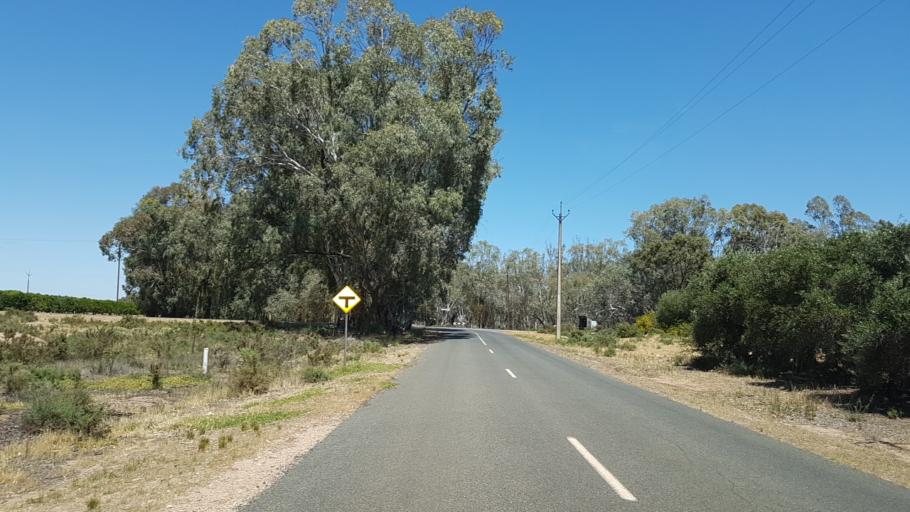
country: AU
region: South Australia
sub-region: Loxton Waikerie
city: Waikerie
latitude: -34.1668
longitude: 140.0272
